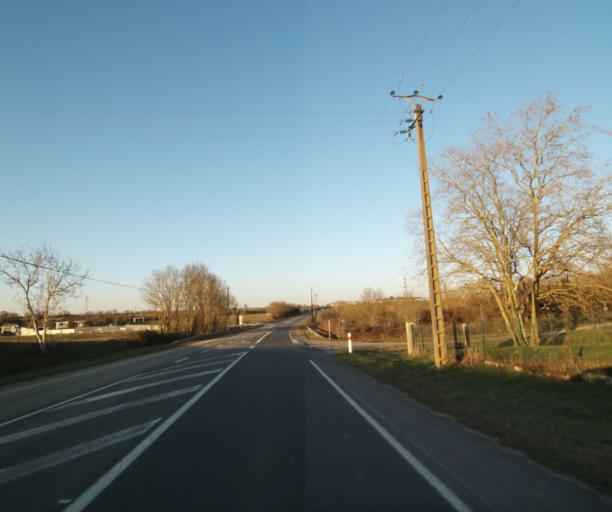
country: FR
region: Poitou-Charentes
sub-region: Departement des Deux-Sevres
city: Niort
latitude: 46.3546
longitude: -0.4388
